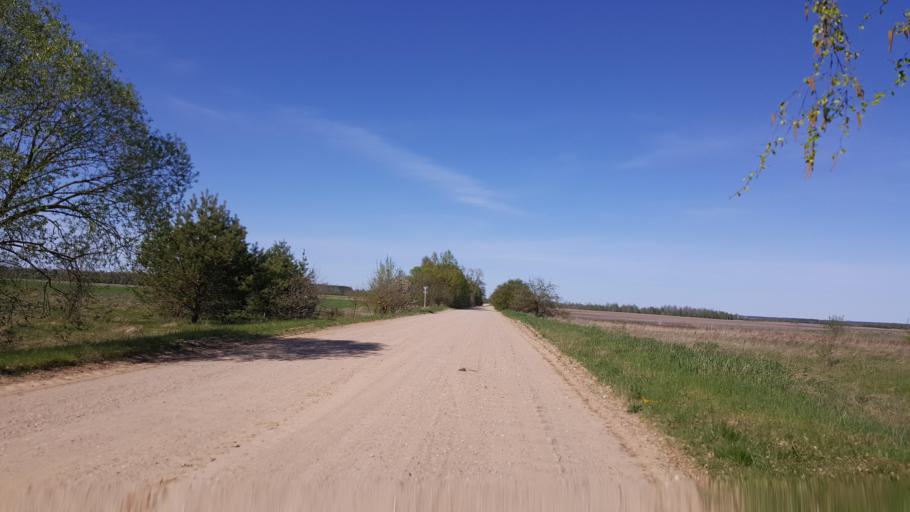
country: BY
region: Brest
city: Kamyanyets
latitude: 52.4234
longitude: 23.8786
